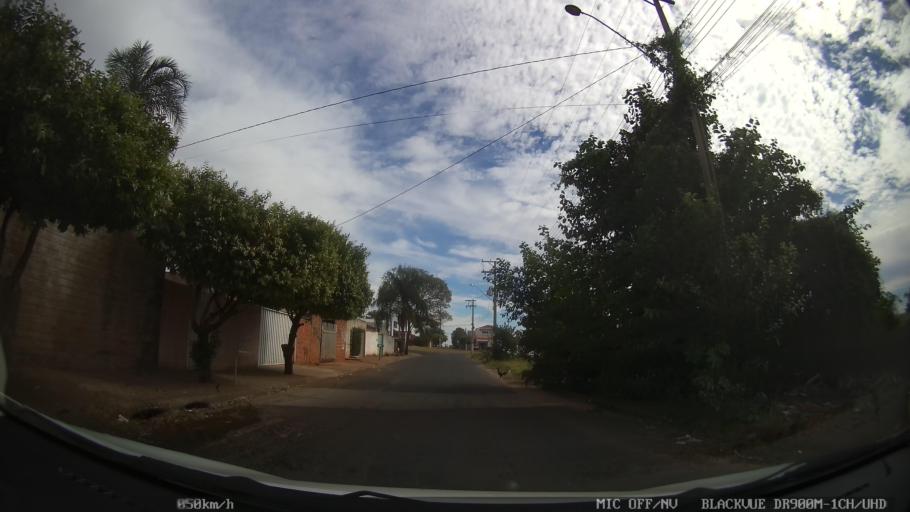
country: BR
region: Sao Paulo
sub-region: Catanduva
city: Catanduva
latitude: -21.1618
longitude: -48.9694
